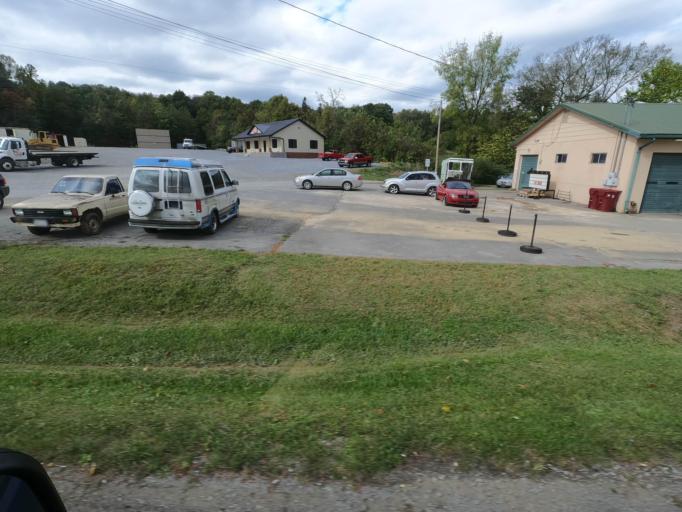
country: US
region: Tennessee
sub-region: Carter County
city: Central
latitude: 36.3261
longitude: -82.3163
